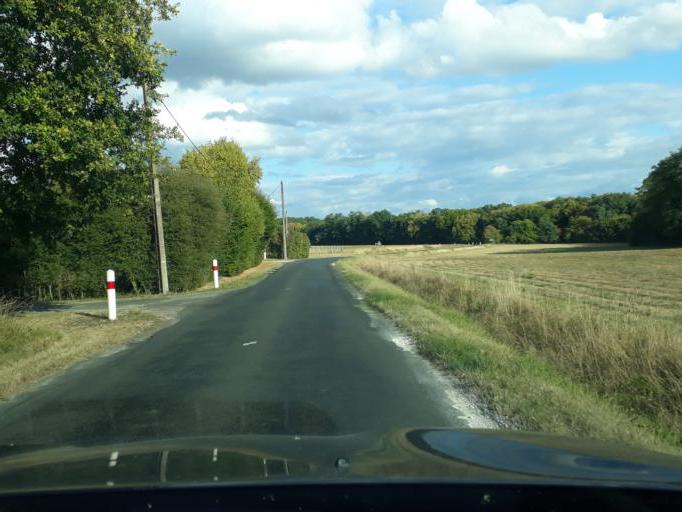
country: FR
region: Centre
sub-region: Departement du Loiret
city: Trainou
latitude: 47.9767
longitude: 2.1296
